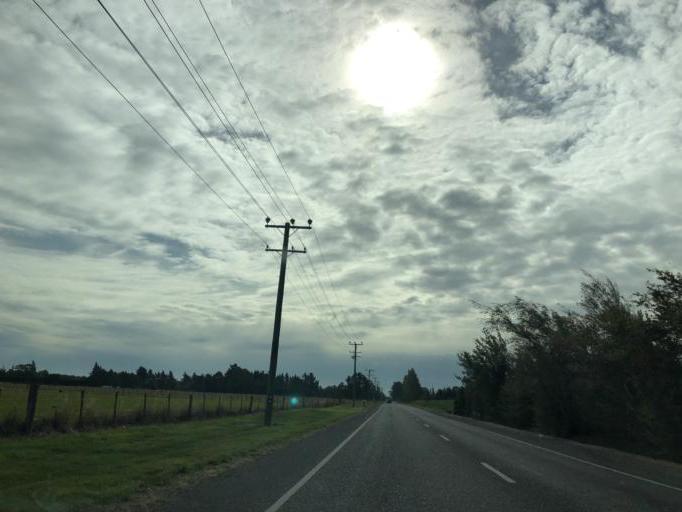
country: NZ
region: Canterbury
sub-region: Selwyn District
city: Rolleston
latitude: -43.6282
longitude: 172.4239
